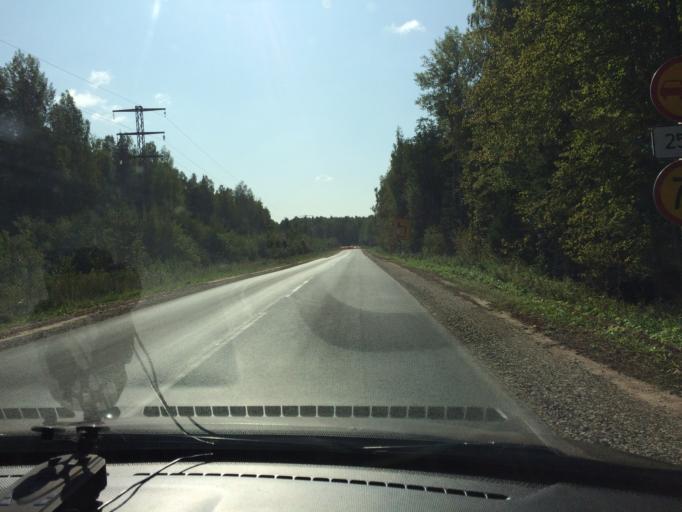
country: RU
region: Mariy-El
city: Surok
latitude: 56.5535
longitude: 48.3137
